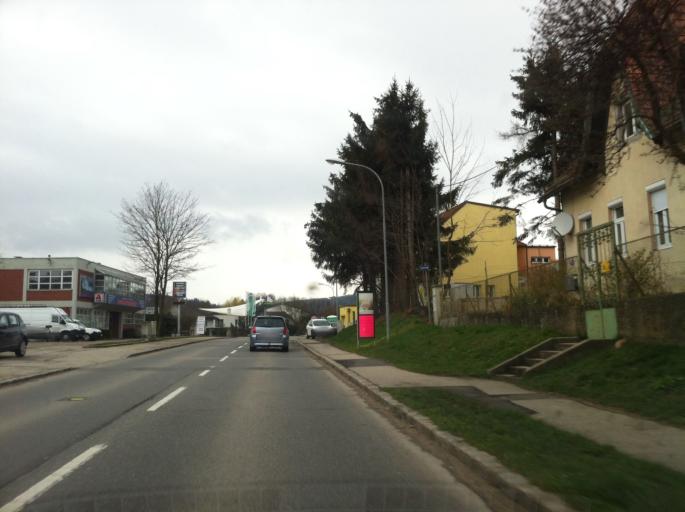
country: AT
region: Lower Austria
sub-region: Politischer Bezirk Wien-Umgebung
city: Gablitz
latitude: 48.2322
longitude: 16.1467
